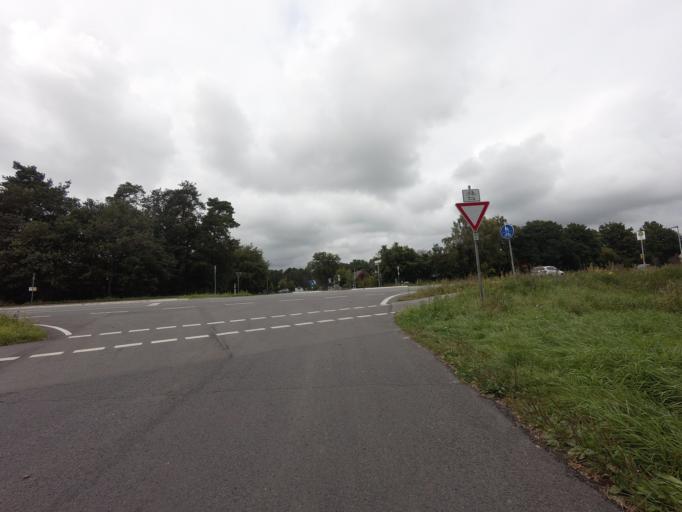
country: NL
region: Overijssel
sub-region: Gemeente Losser
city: Losser
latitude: 52.2639
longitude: 7.0517
